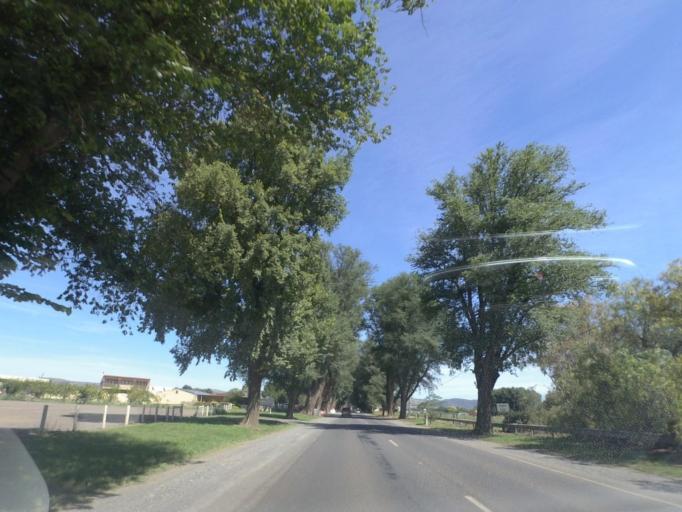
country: AU
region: Victoria
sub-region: Moorabool
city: Bacchus Marsh
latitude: -37.6815
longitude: 144.4584
